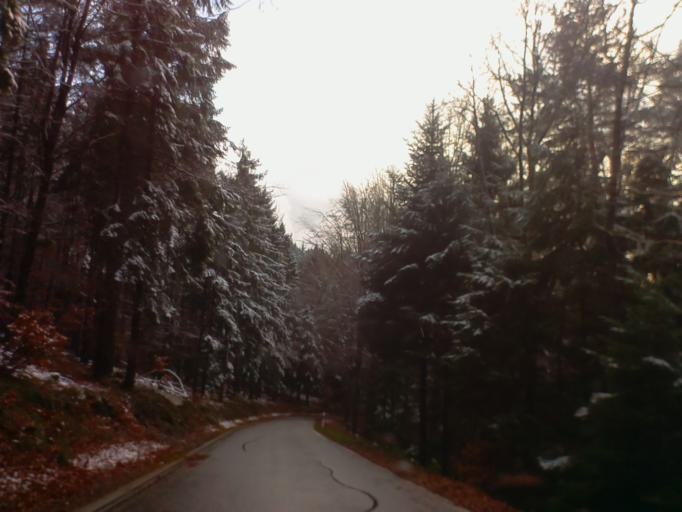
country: DE
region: Hesse
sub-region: Regierungsbezirk Darmstadt
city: Wald-Michelbach
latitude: 49.5549
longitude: 8.8812
